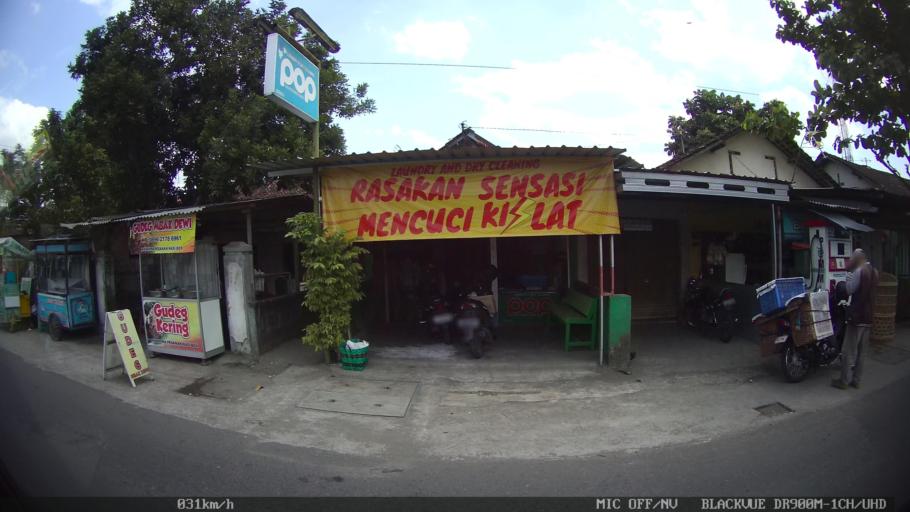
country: ID
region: Daerah Istimewa Yogyakarta
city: Kasihan
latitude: -7.8184
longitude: 110.3482
